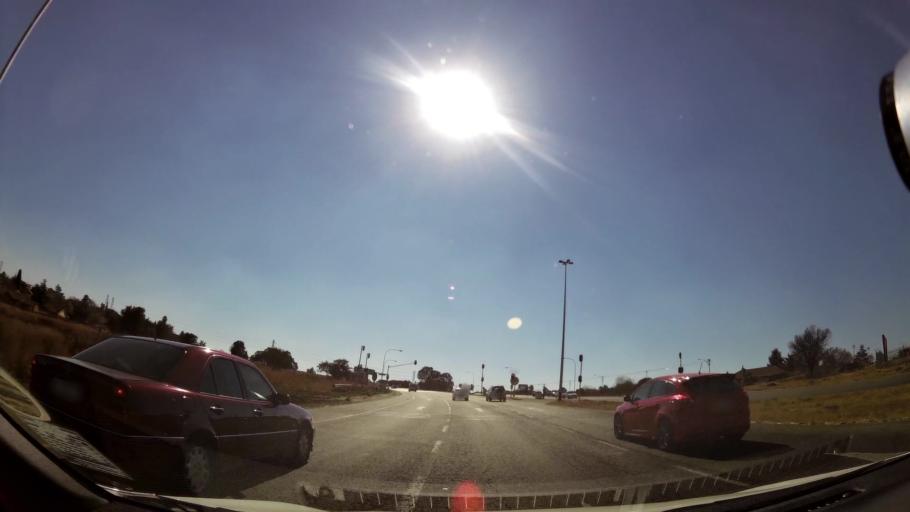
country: ZA
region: Gauteng
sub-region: City of Johannesburg Metropolitan Municipality
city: Johannesburg
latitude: -26.2783
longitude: 28.0344
